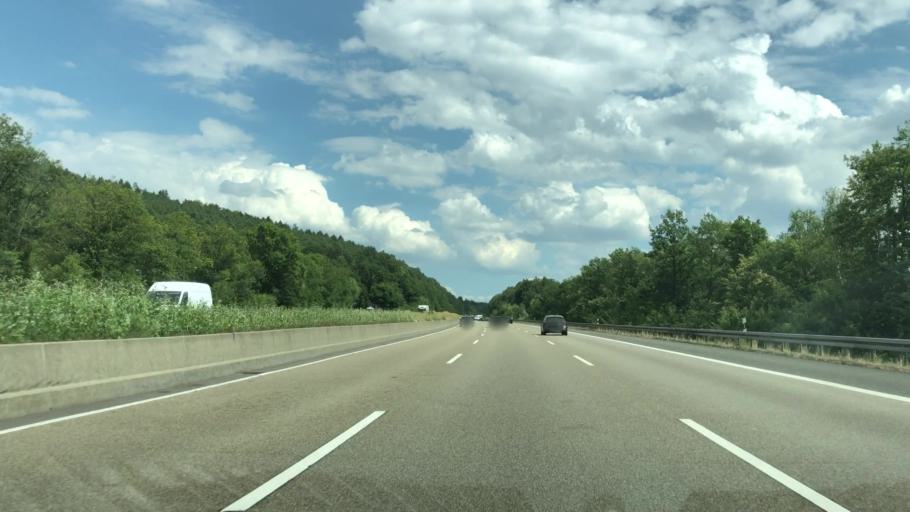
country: DE
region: Hesse
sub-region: Regierungsbezirk Kassel
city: Niederaula
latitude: 50.7618
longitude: 9.5971
